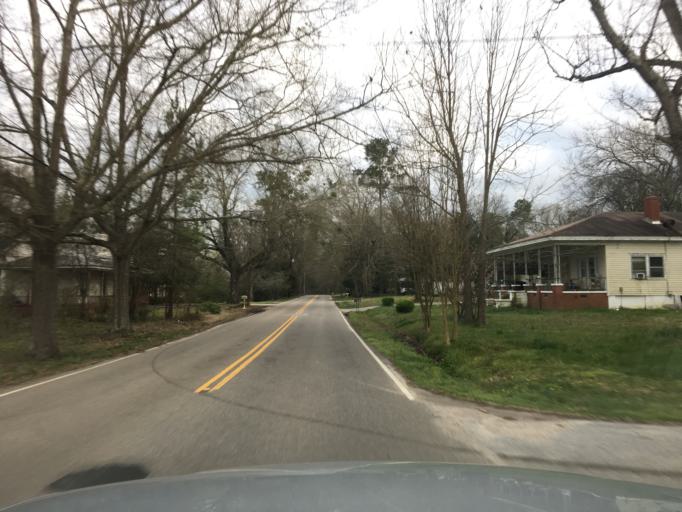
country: US
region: South Carolina
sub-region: Saluda County
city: Saluda
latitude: 33.9977
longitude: -81.7729
